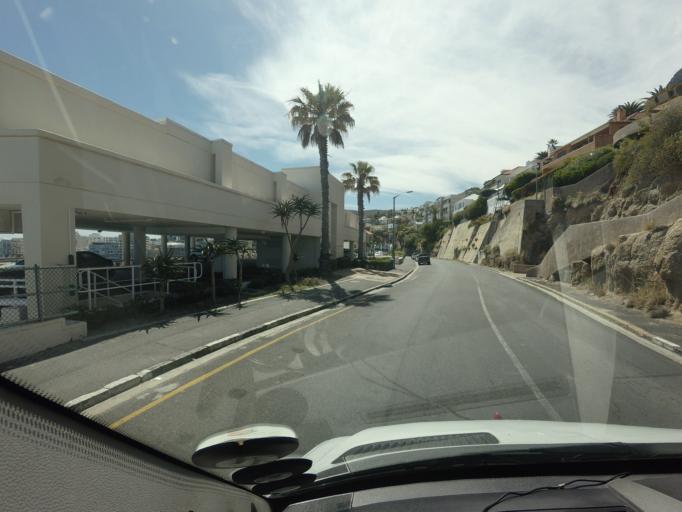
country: ZA
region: Western Cape
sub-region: City of Cape Town
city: Cape Town
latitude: -33.9282
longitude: 18.3761
